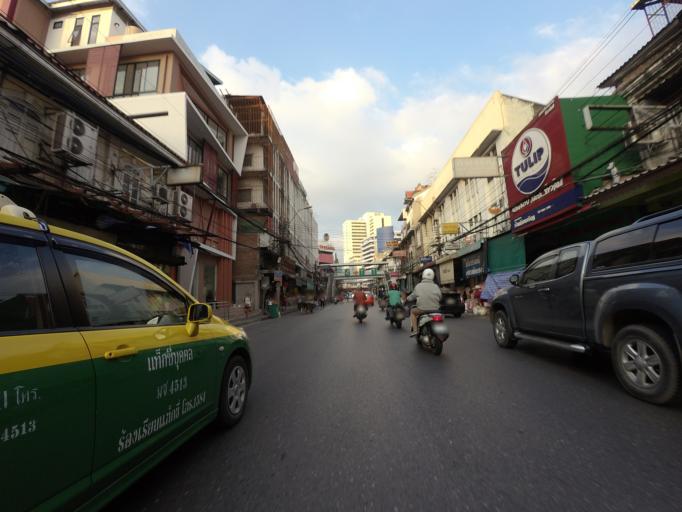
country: TH
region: Bangkok
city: Bangkok
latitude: 13.7438
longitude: 100.5018
